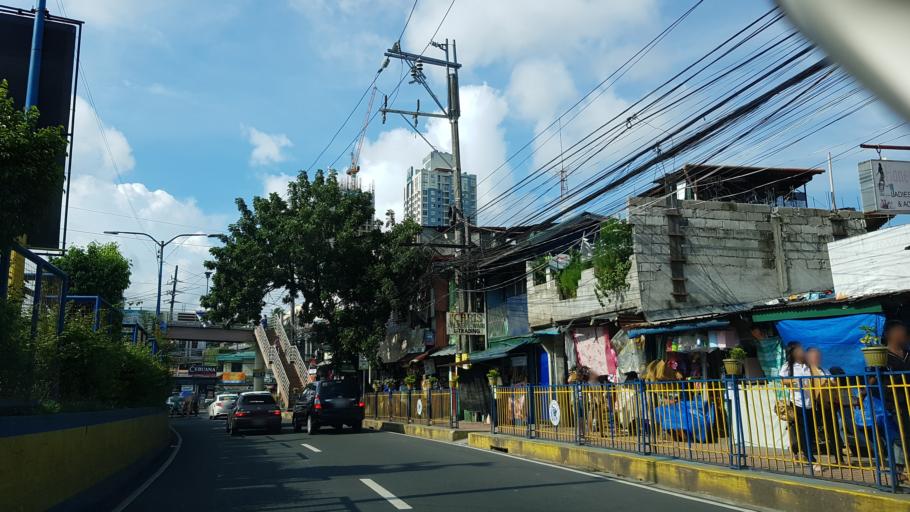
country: PH
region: Metro Manila
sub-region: Mandaluyong
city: Mandaluyong City
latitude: 14.5870
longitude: 121.0379
